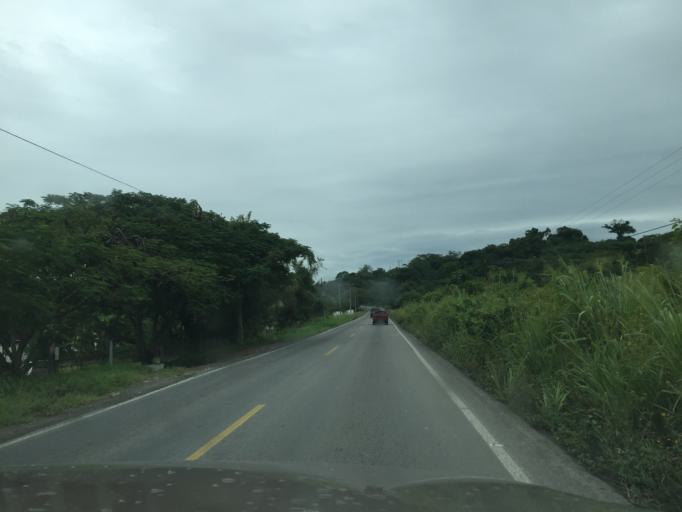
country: MX
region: Veracruz
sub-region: Papantla
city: El Chote
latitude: 20.4388
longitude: -97.3940
